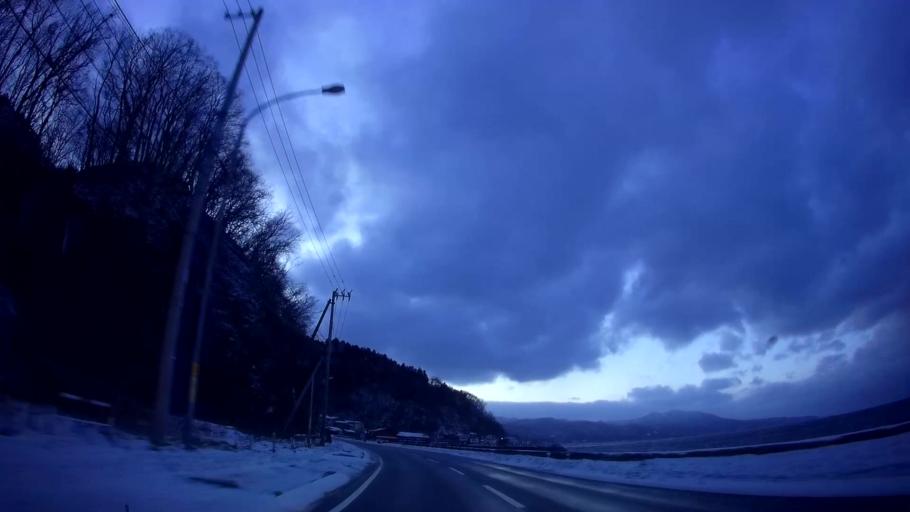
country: JP
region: Hokkaido
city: Hakodate
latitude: 41.8933
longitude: 141.0450
